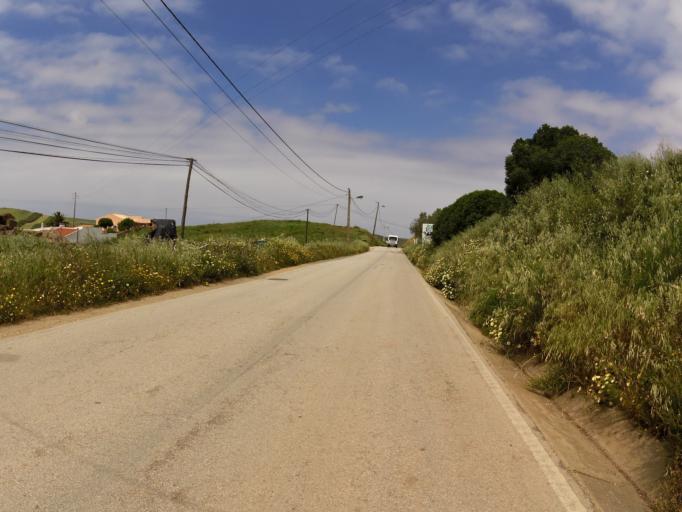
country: PT
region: Faro
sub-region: Vila do Bispo
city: Vila do Bispo
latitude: 37.0796
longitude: -8.8880
